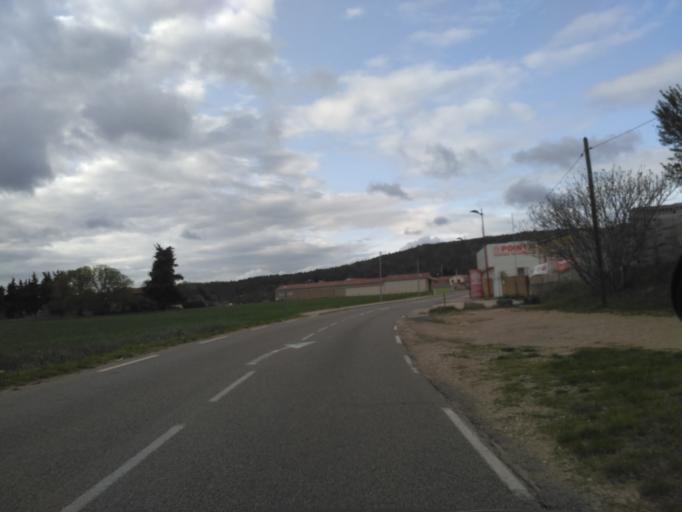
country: FR
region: Provence-Alpes-Cote d'Azur
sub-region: Departement du Var
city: Barjols
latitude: 43.5884
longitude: 6.0131
